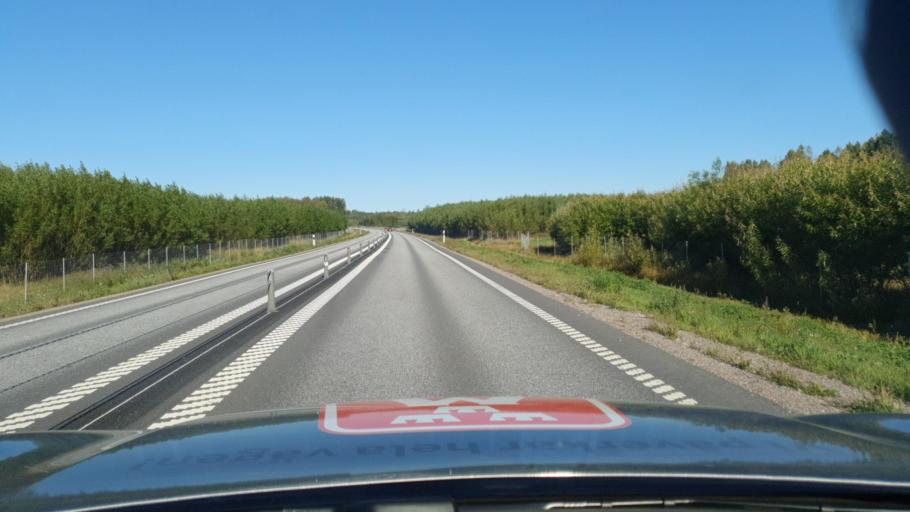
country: SE
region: OErebro
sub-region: Hallsbergs Kommun
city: Palsboda
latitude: 59.0403
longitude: 15.3512
